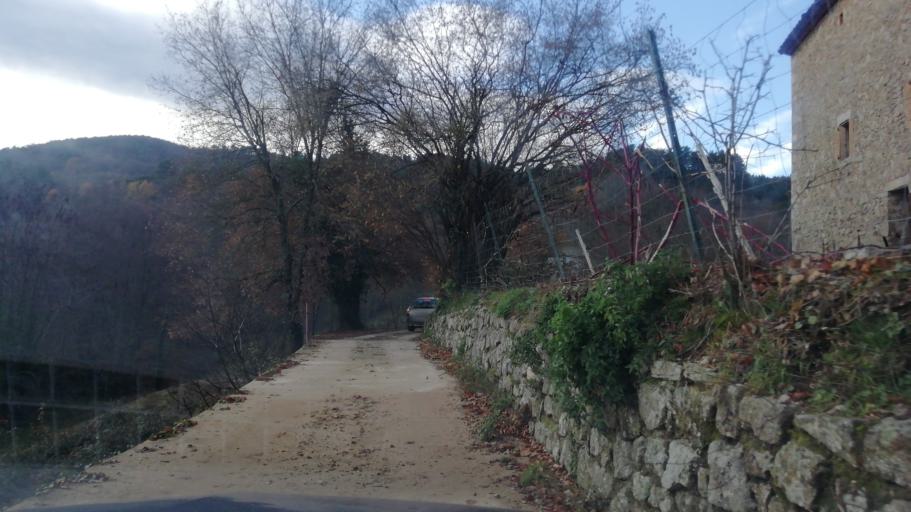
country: FR
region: Languedoc-Roussillon
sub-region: Departement du Gard
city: Lasalle
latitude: 44.0309
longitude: 3.8562
